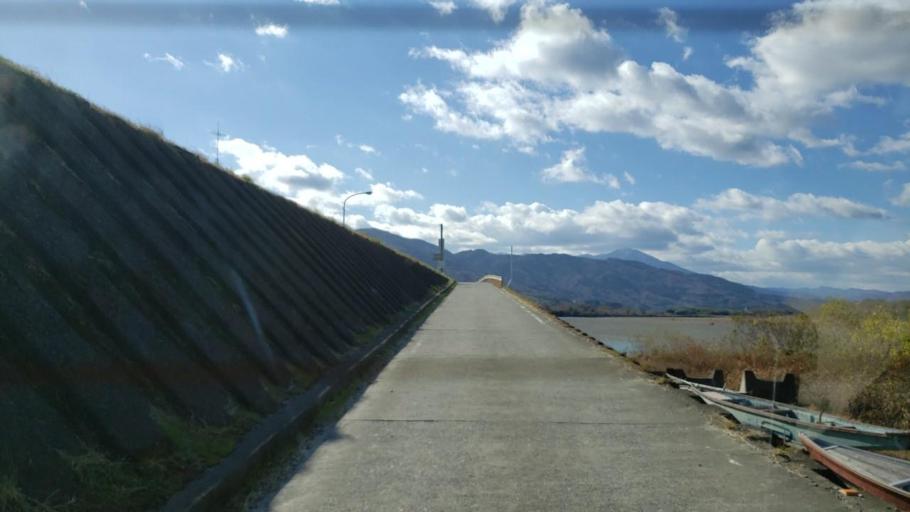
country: JP
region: Tokushima
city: Kamojimacho-jogejima
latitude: 34.0673
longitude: 134.3181
